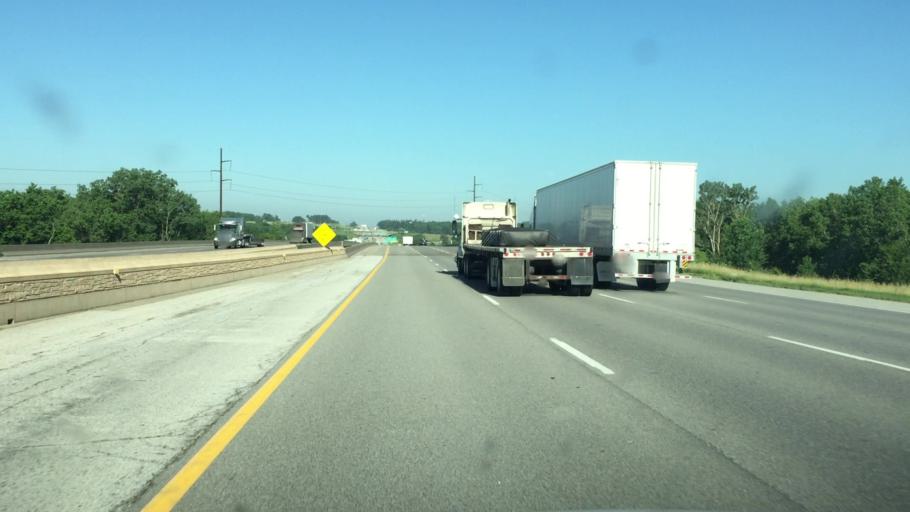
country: US
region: Iowa
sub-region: Johnson County
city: Coralville
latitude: 41.6943
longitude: -91.6181
